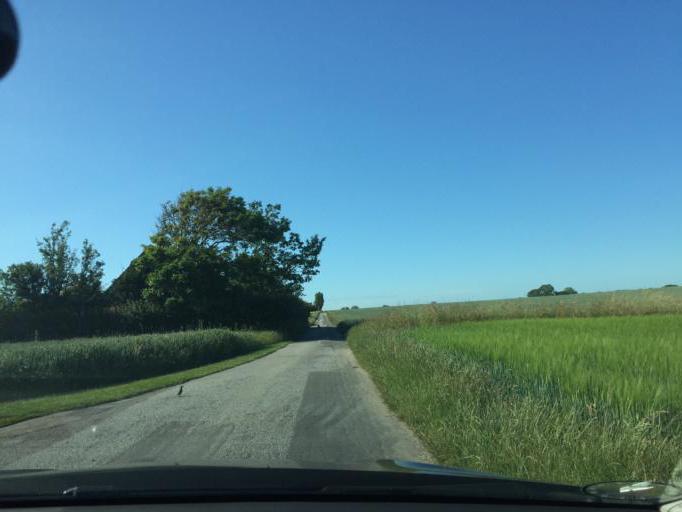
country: DK
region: Zealand
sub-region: Slagelse Kommune
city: Skaelskor
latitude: 55.1996
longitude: 11.1821
